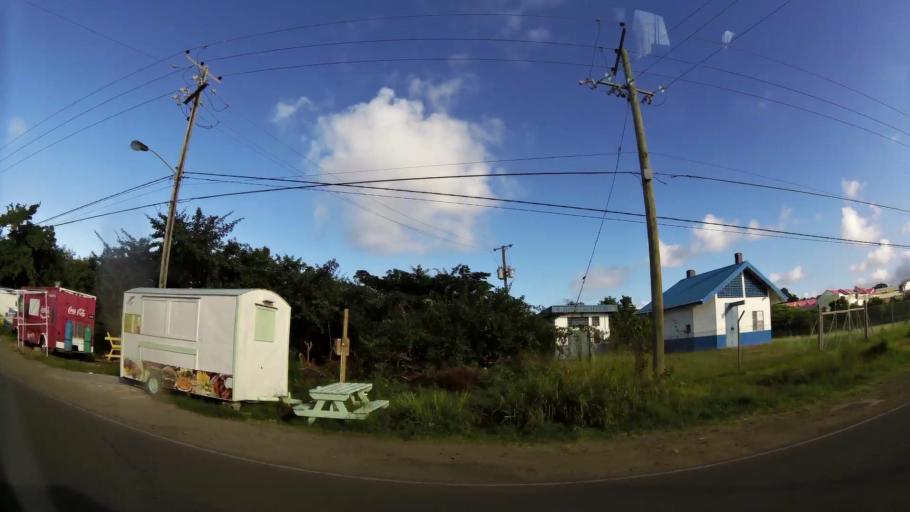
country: LC
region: Gros-Islet
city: Gros Islet
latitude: 14.0790
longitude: -60.9478
